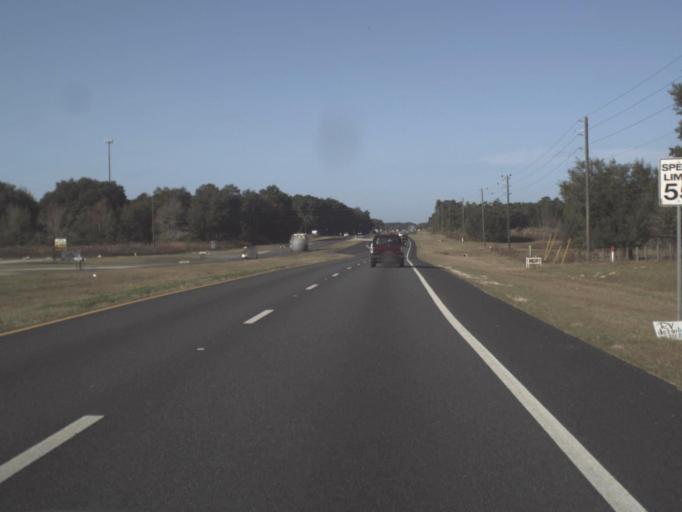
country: US
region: Florida
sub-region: Marion County
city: Belleview
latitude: 29.0260
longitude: -82.1211
